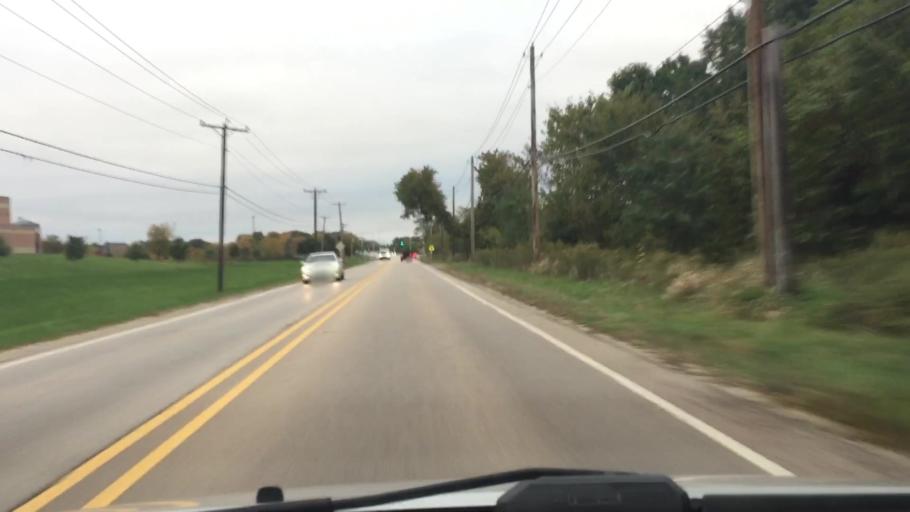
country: US
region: Illinois
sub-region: Kane County
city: Farmington
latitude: 41.9464
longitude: -88.3181
